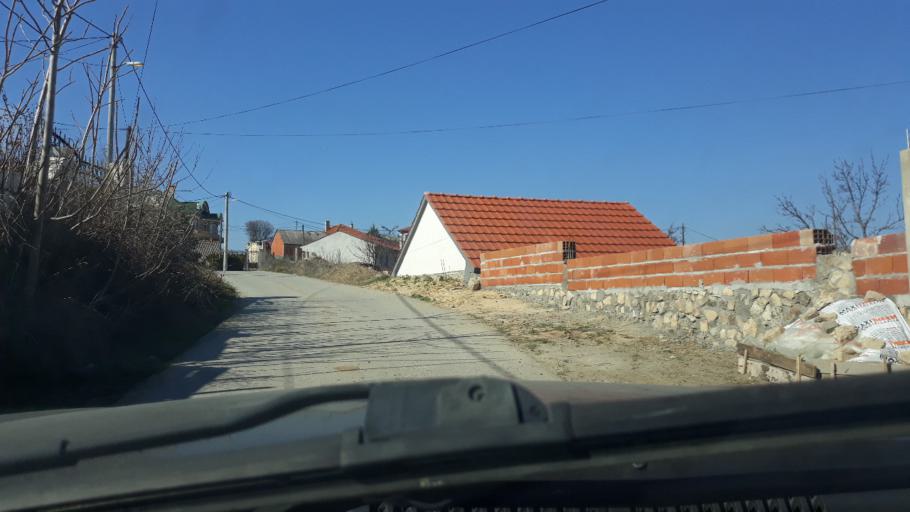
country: MK
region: Veles
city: Gorno Orizari
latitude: 41.6821
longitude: 21.7341
